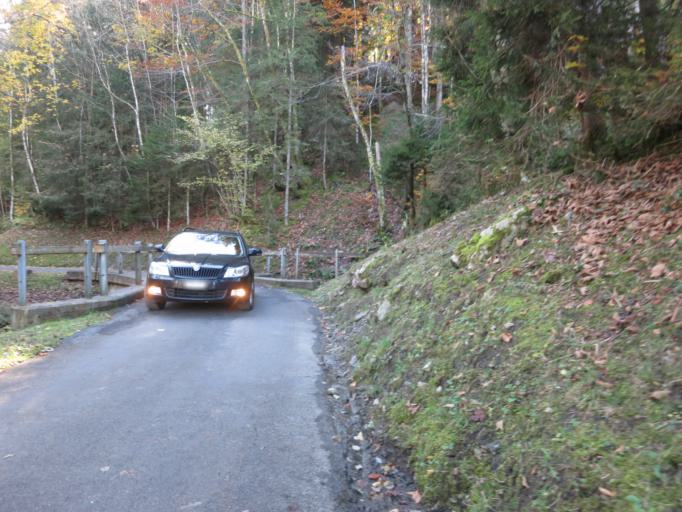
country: CH
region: Schwyz
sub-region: Bezirk March
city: Vorderthal
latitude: 47.0758
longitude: 8.9122
